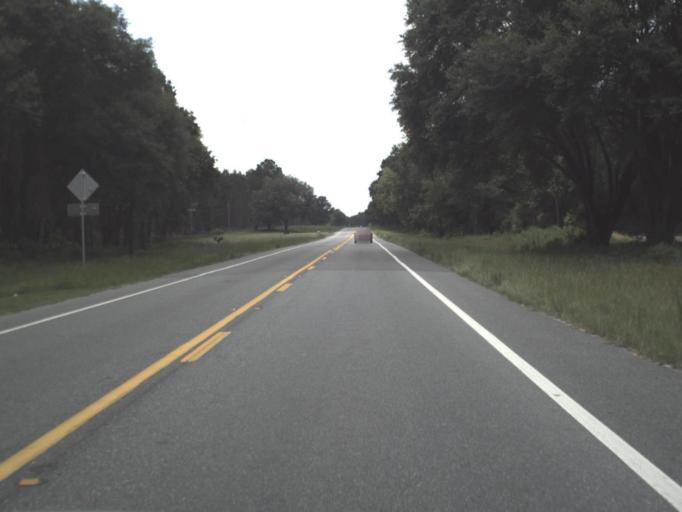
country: US
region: Florida
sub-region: Columbia County
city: Five Points
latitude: 30.3022
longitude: -82.7096
